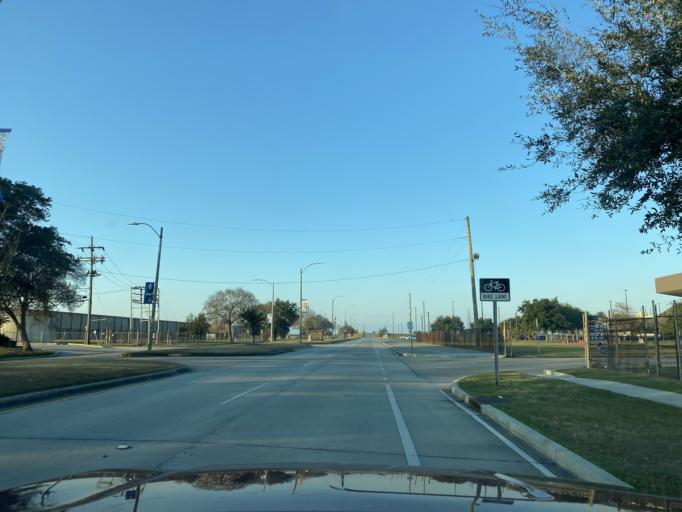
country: US
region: Louisiana
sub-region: Orleans Parish
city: New Orleans
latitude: 30.0283
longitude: -90.0522
